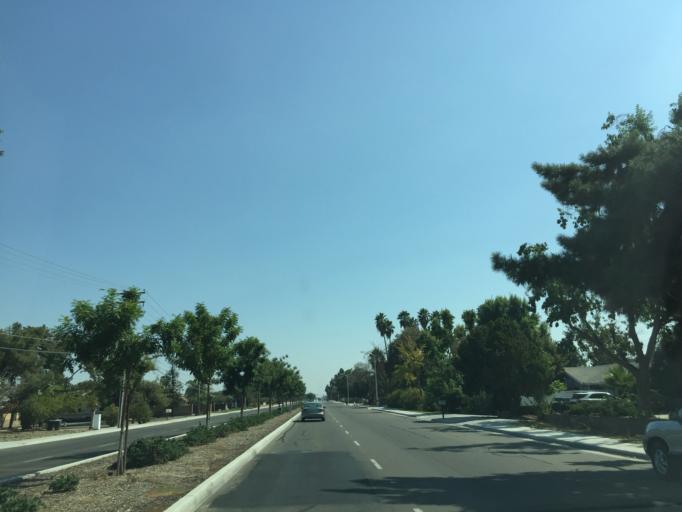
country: US
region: California
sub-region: Kings County
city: Lucerne
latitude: 36.3497
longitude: -119.6729
